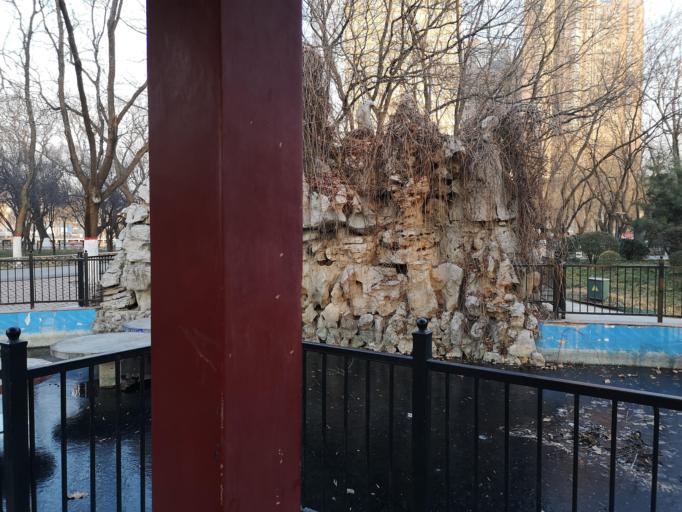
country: CN
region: Henan Sheng
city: Zhongyuanlu
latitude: 35.7742
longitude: 115.0774
